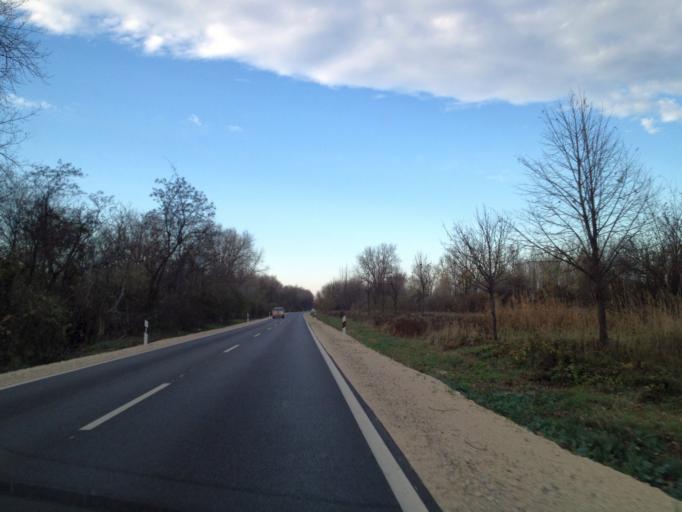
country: HU
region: Gyor-Moson-Sopron
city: Nyul
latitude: 47.6079
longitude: 17.6852
